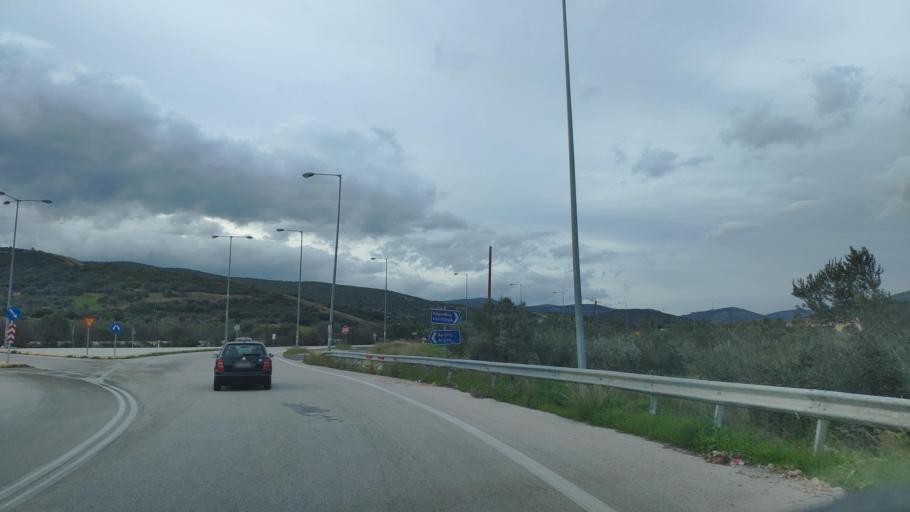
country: GR
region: Peloponnese
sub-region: Nomos Argolidos
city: Koutsopodi
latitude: 37.7531
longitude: 22.7344
